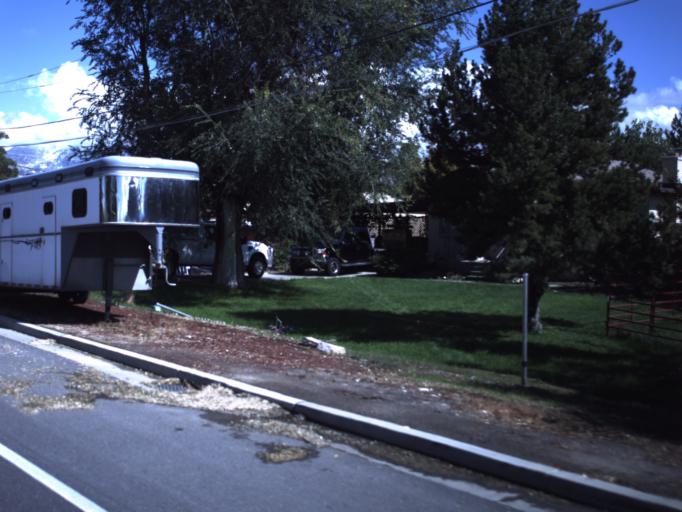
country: US
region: Utah
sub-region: Utah County
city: Spanish Fork
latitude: 40.0959
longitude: -111.6554
